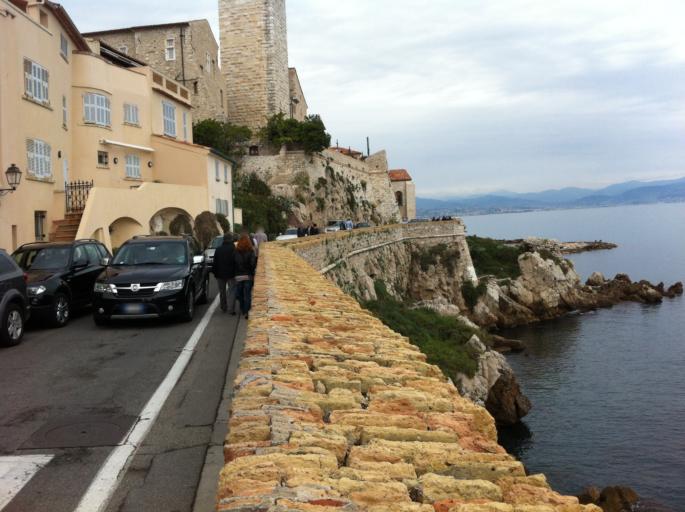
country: FR
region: Provence-Alpes-Cote d'Azur
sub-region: Departement des Alpes-Maritimes
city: Antibes
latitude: 43.5800
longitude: 7.1281
